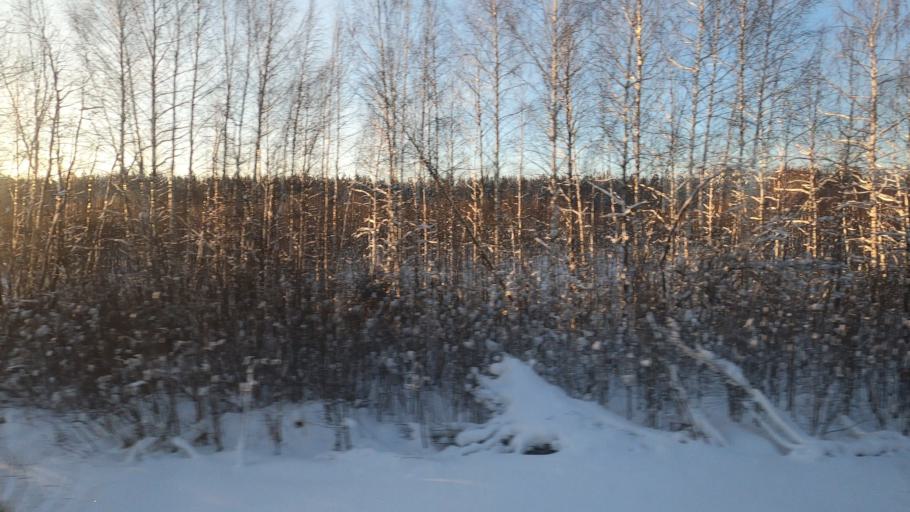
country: RU
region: Moskovskaya
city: Taldom
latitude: 56.6540
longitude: 37.5662
